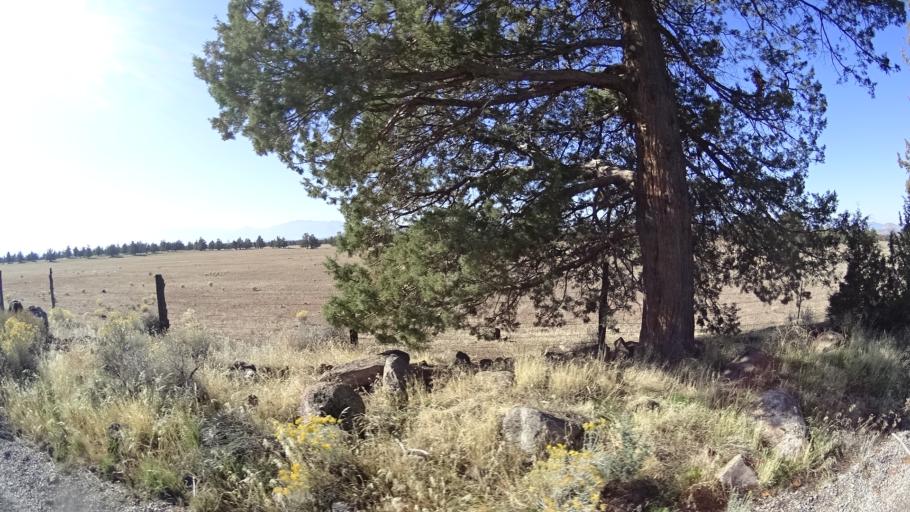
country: US
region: California
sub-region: Siskiyou County
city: Weed
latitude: 41.6311
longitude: -122.3347
